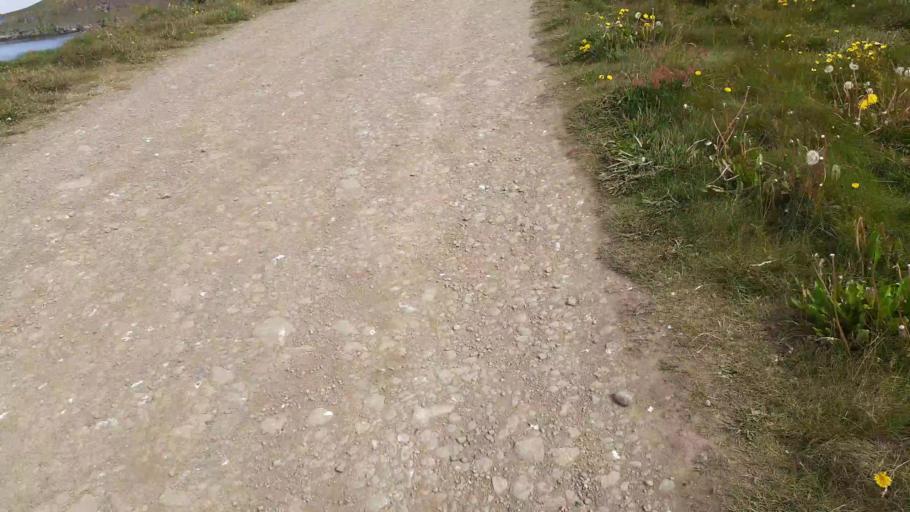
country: IS
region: Northeast
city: Dalvik
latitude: 66.5514
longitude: -18.0236
